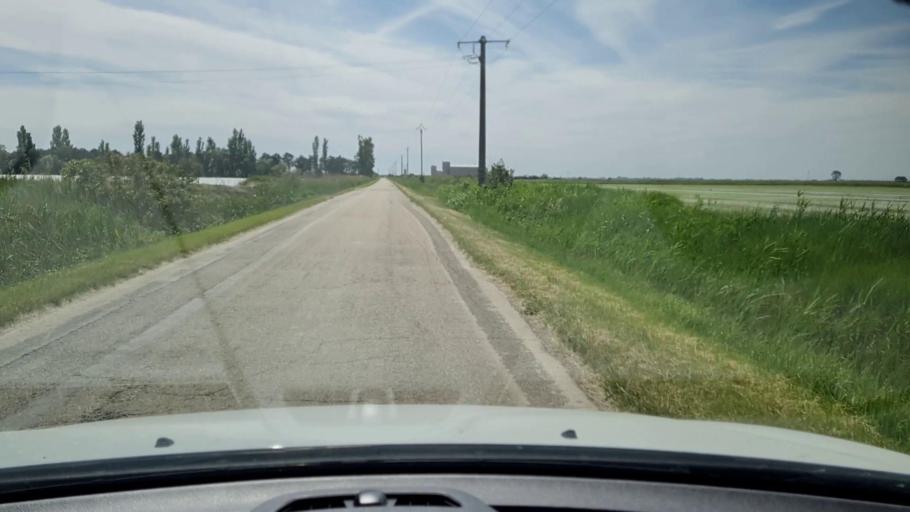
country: FR
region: Languedoc-Roussillon
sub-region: Departement du Gard
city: Saint-Gilles
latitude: 43.5886
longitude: 4.4248
